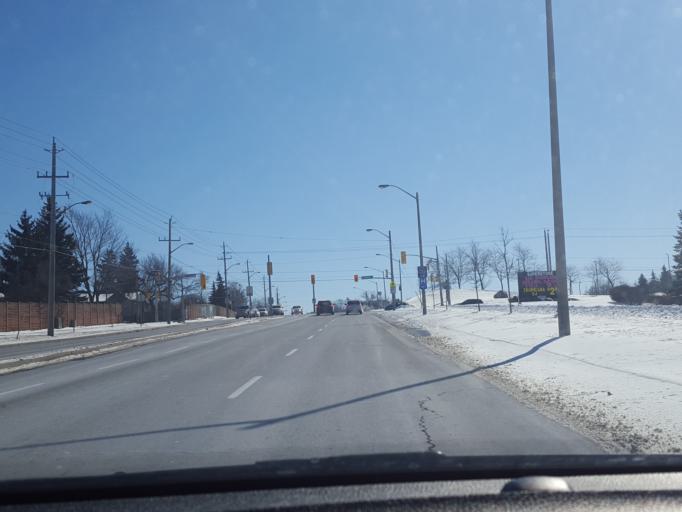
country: CA
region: Ontario
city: Kitchener
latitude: 43.4297
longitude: -80.5244
